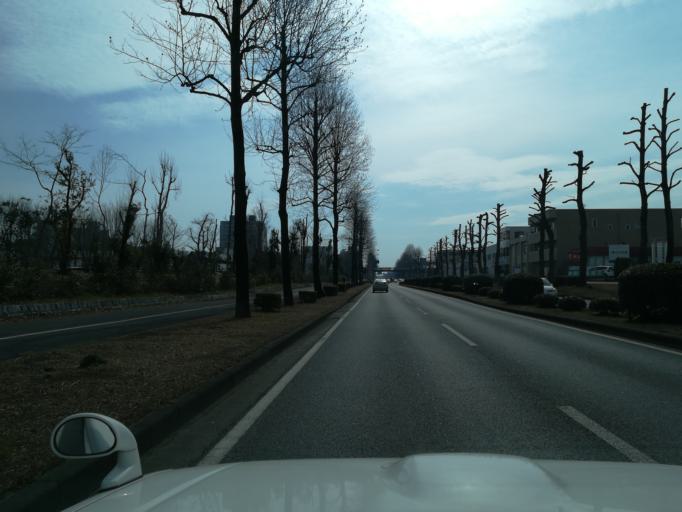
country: JP
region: Ibaraki
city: Naka
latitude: 36.0918
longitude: 140.1001
